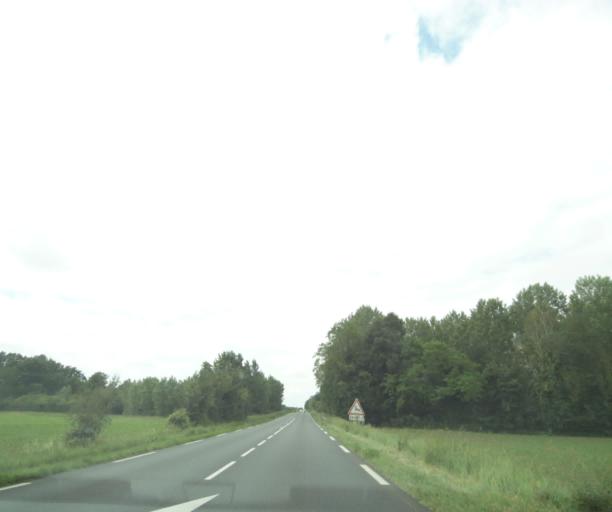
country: FR
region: Pays de la Loire
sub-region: Departement de Maine-et-Loire
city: Montreuil-Bellay
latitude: 47.1088
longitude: -0.1647
